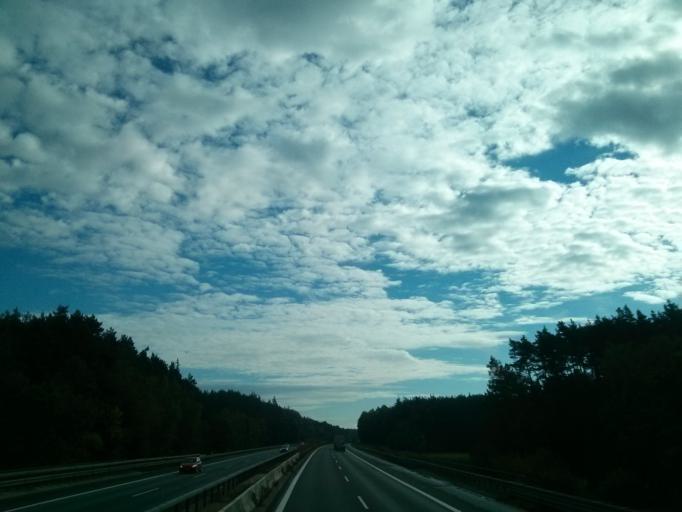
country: DE
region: Bavaria
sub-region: Regierungsbezirk Mittelfranken
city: Rohr
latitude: 49.3157
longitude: 10.8816
